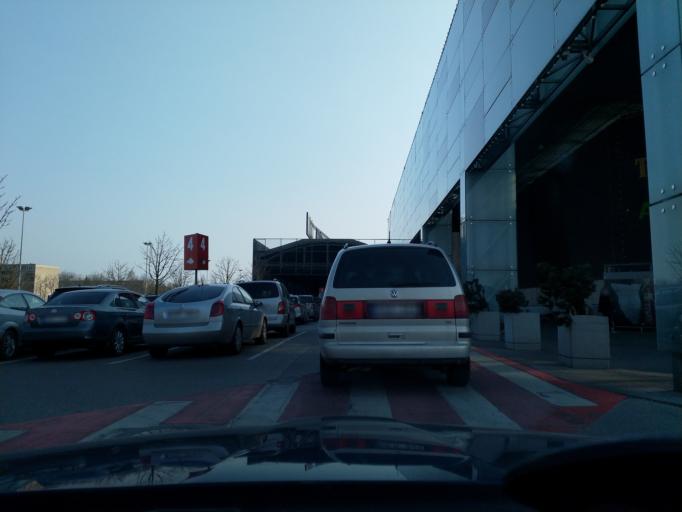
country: LT
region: Klaipedos apskritis
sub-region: Klaipeda
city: Klaipeda
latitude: 55.6931
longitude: 21.1537
